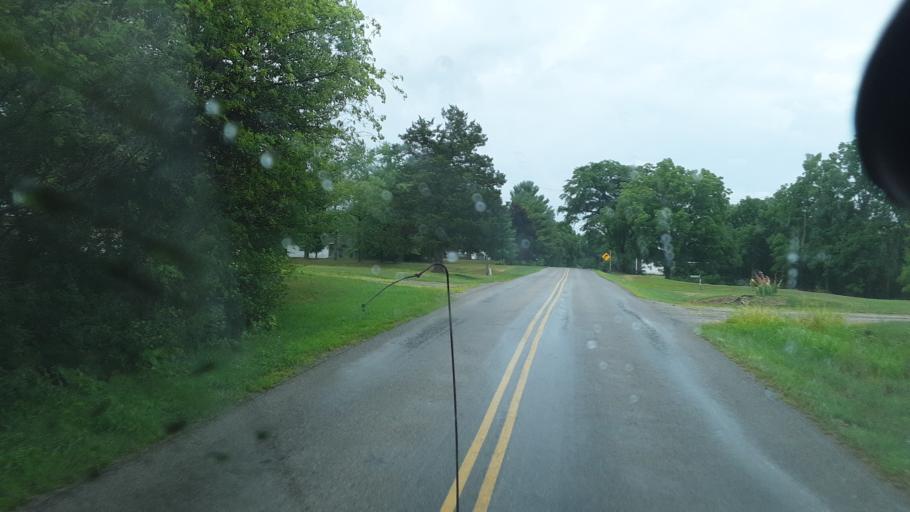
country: US
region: Indiana
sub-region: Steuben County
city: Hamilton
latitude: 41.6374
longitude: -84.7902
